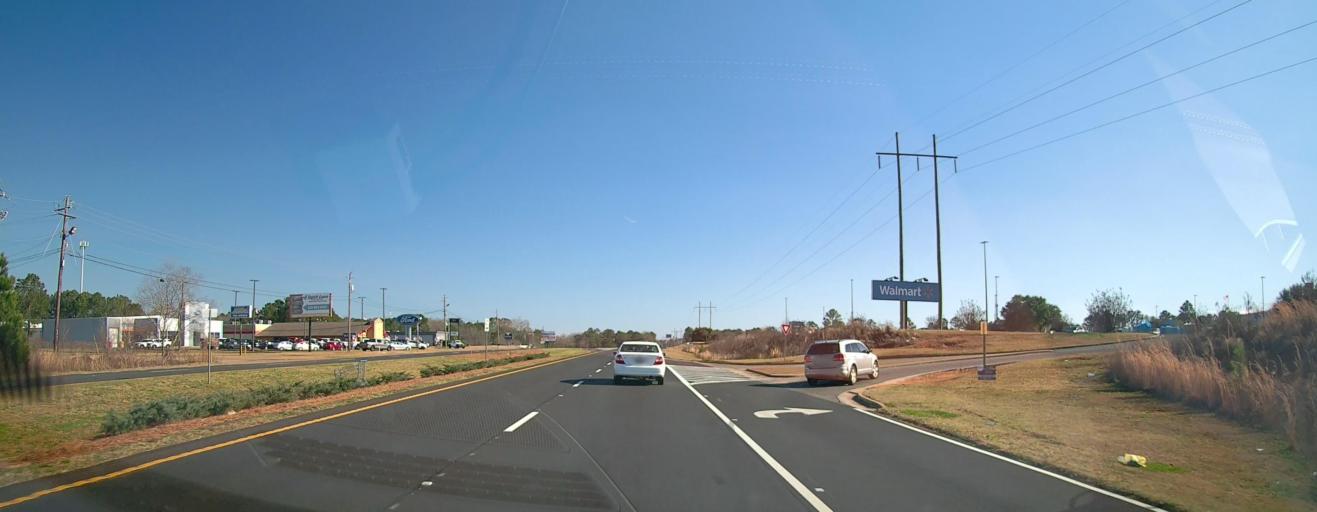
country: US
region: Georgia
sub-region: Sumter County
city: Americus
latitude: 32.0622
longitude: -84.2010
